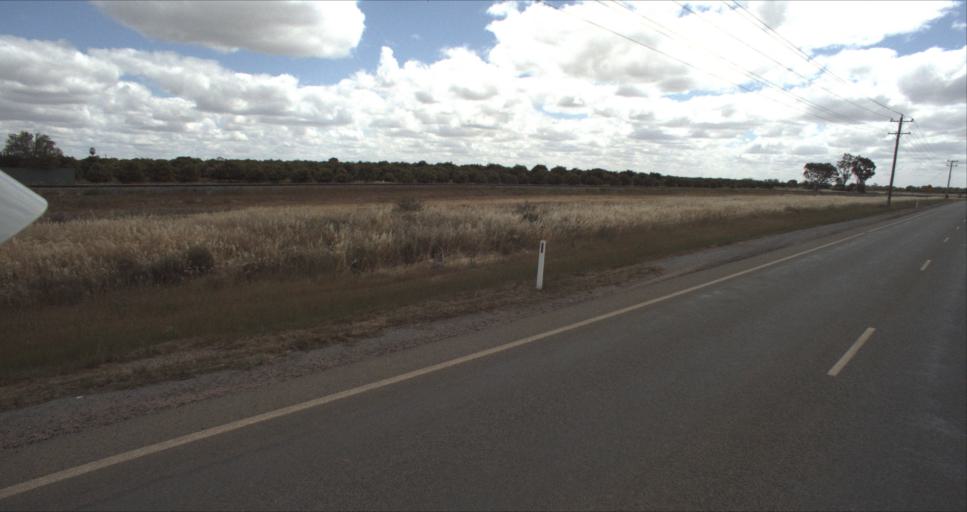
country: AU
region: New South Wales
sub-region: Leeton
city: Leeton
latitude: -34.5779
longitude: 146.3970
